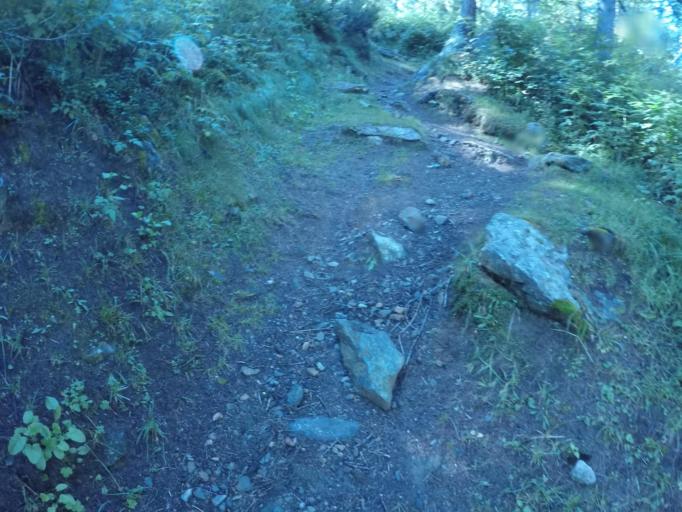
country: IT
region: Aosta Valley
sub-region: Valle d'Aosta
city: Paquier
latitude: 45.8747
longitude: 7.6375
